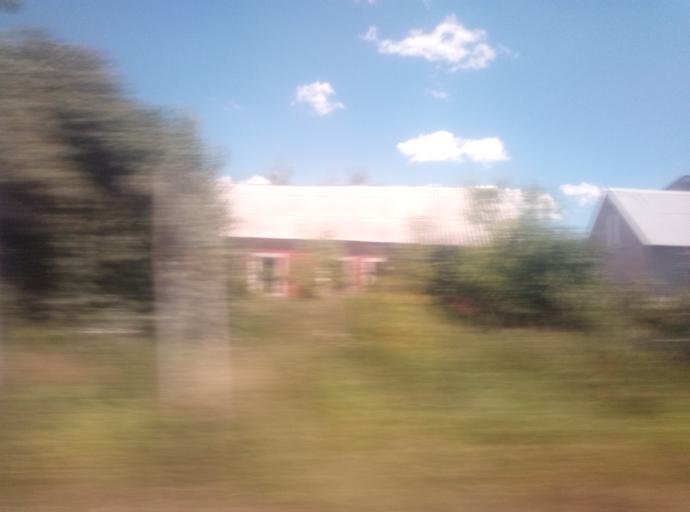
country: RU
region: Tula
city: Kireyevsk
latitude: 53.9708
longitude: 37.9309
